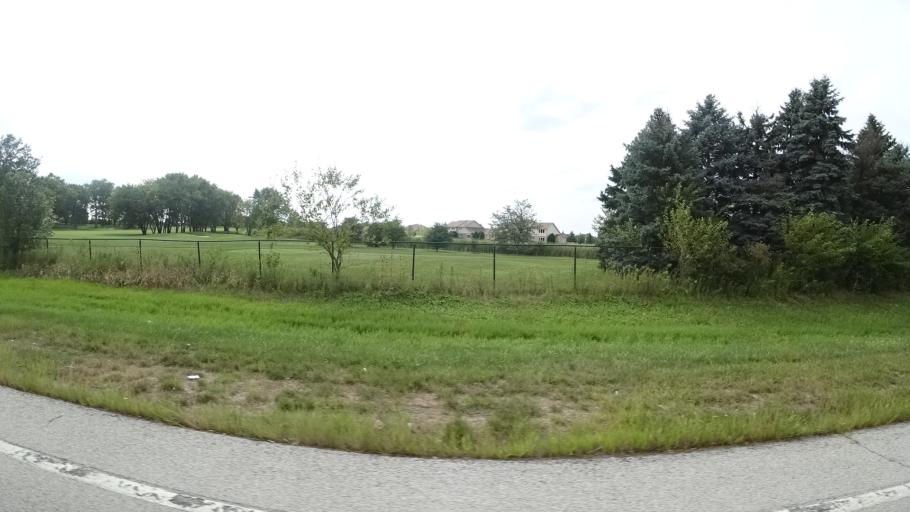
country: US
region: Illinois
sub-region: Will County
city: Frankfort Square
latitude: 41.5299
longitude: -87.7711
